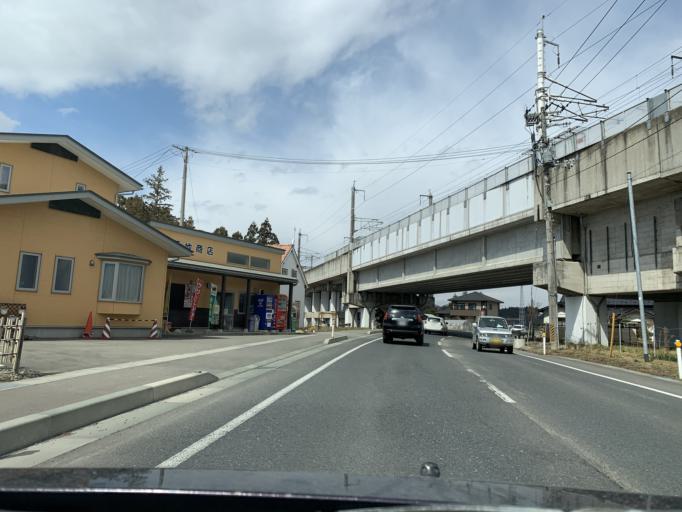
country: JP
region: Iwate
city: Kitakami
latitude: 39.2247
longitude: 141.1279
